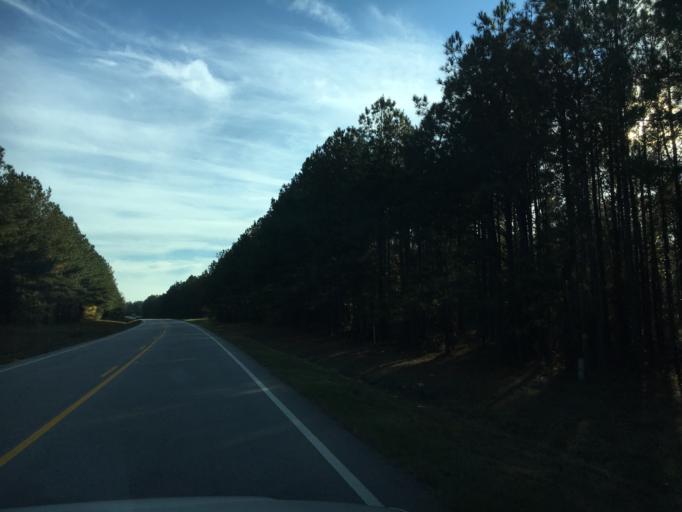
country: US
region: Georgia
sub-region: Elbert County
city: Elberton
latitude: 33.9547
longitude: -82.7692
